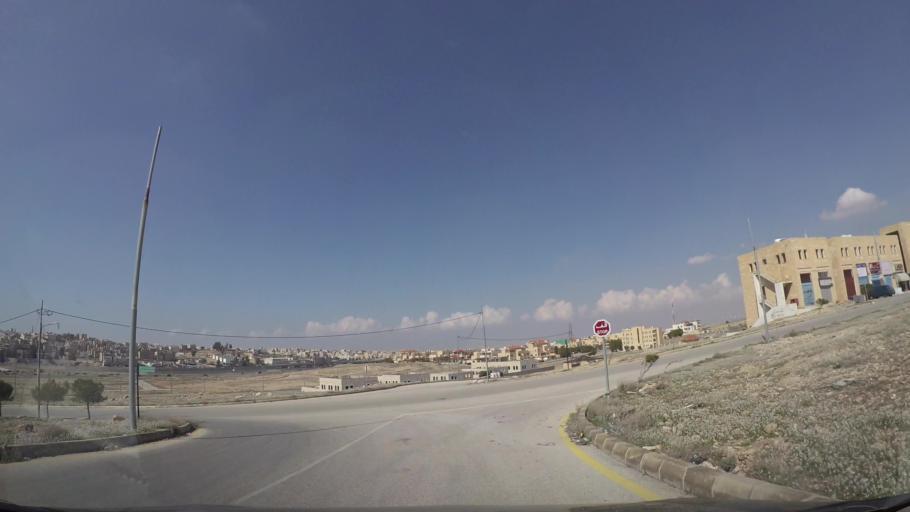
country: JO
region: Zarqa
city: Zarqa
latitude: 32.0744
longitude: 36.1084
